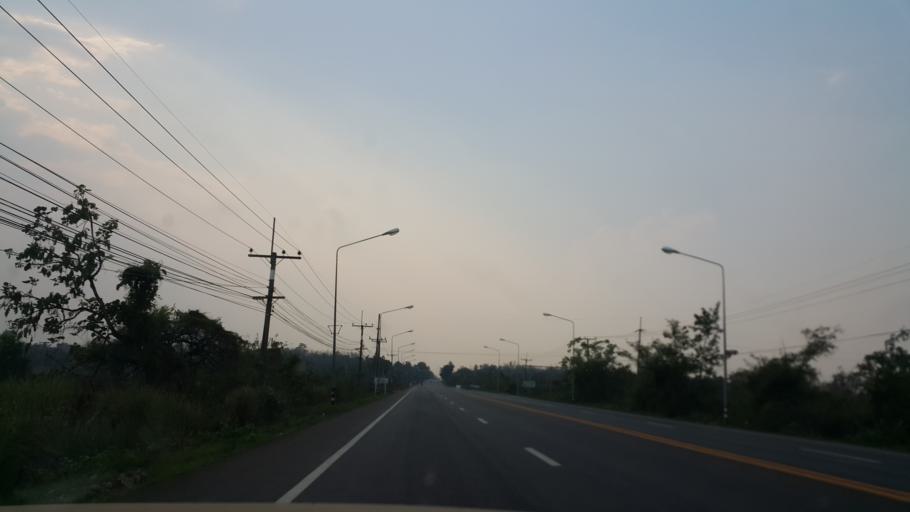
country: TH
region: Nakhon Phanom
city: Renu Nakhon
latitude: 17.0245
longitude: 104.7168
